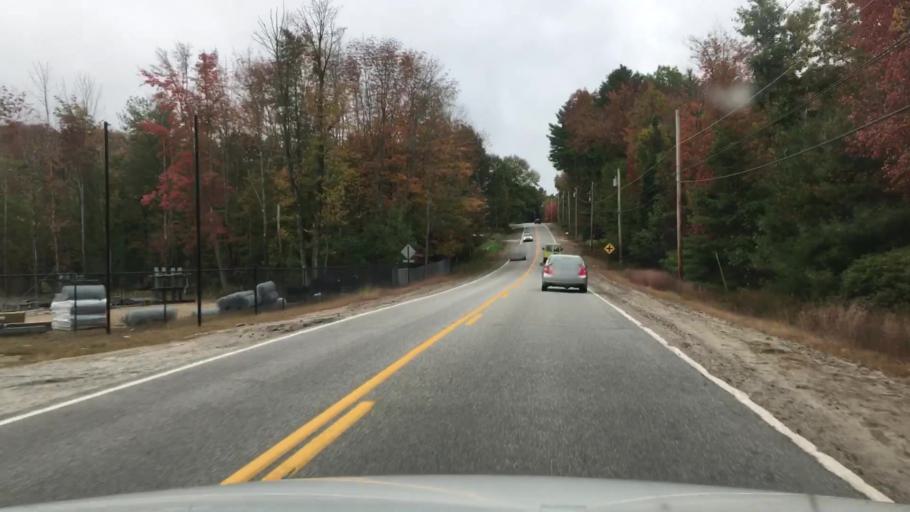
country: US
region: Maine
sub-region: Oxford County
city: Norway
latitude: 44.2213
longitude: -70.5924
